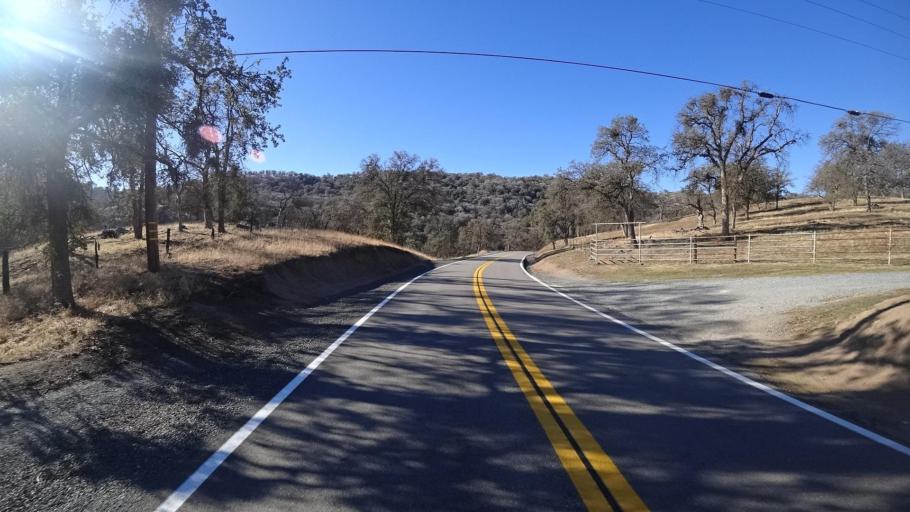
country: US
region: California
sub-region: Kern County
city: Alta Sierra
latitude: 35.7075
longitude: -118.7721
